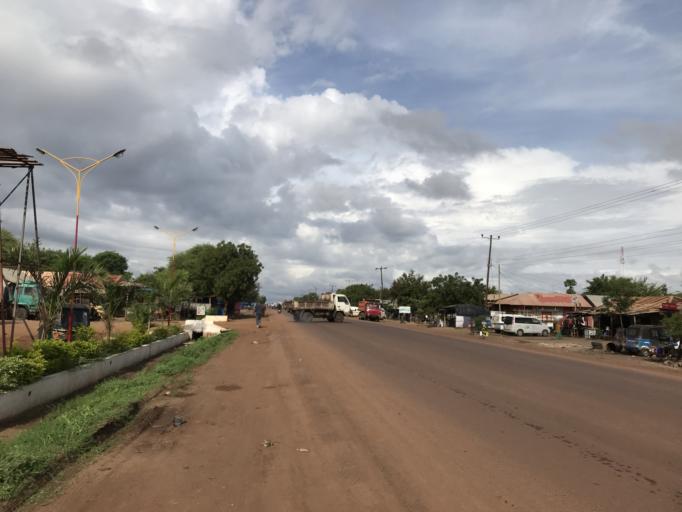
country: TZ
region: Tabora
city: Igunga
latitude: -4.2869
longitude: 33.8829
